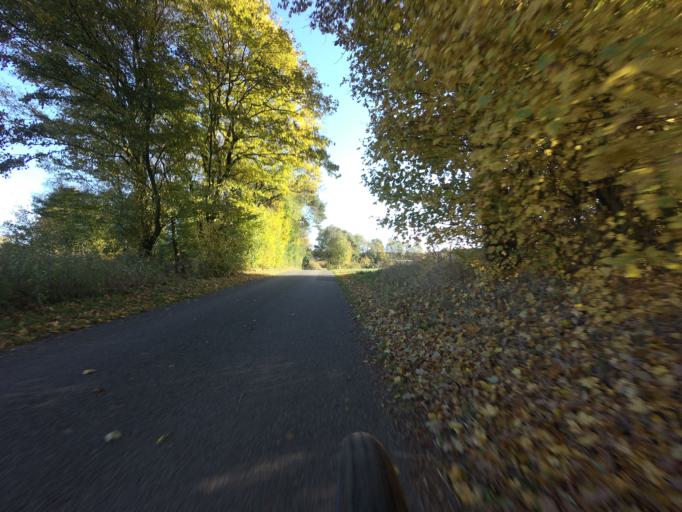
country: DK
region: Central Jutland
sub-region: Norddjurs Kommune
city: Grenaa
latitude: 56.4944
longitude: 10.6997
